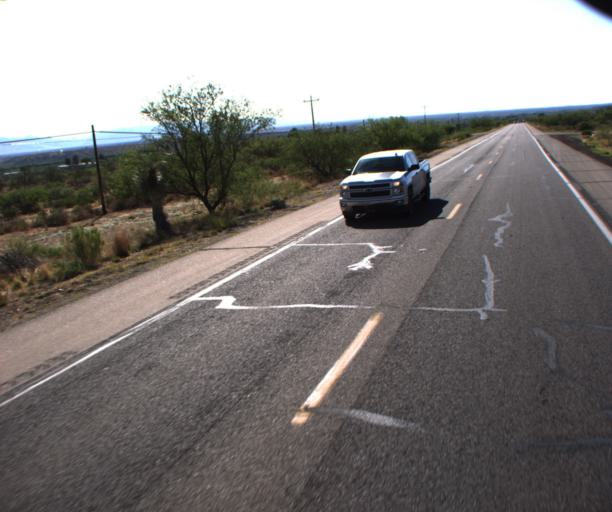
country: US
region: Arizona
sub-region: Cochise County
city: Benson
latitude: 31.9243
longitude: -110.2730
